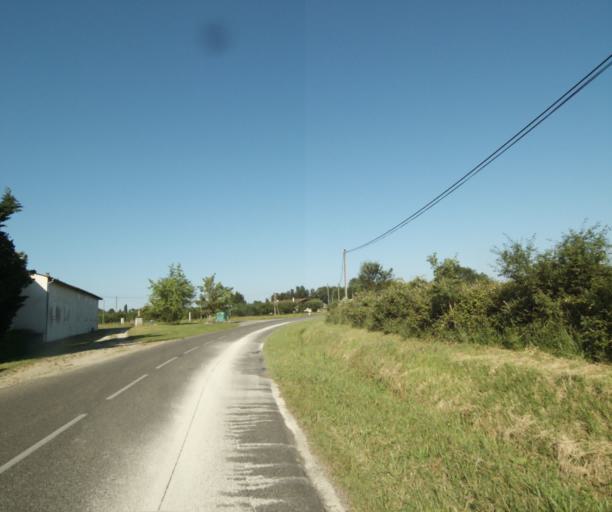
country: FR
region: Midi-Pyrenees
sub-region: Departement du Tarn-et-Garonne
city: Saint-Nauphary
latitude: 44.0158
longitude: 1.4100
